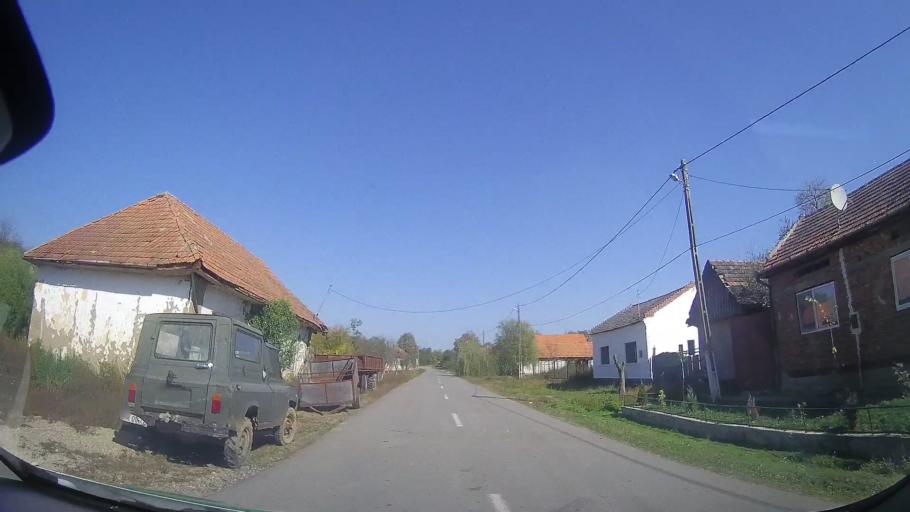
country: RO
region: Timis
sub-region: Comuna Bara
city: Bara
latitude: 45.8957
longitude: 21.8812
